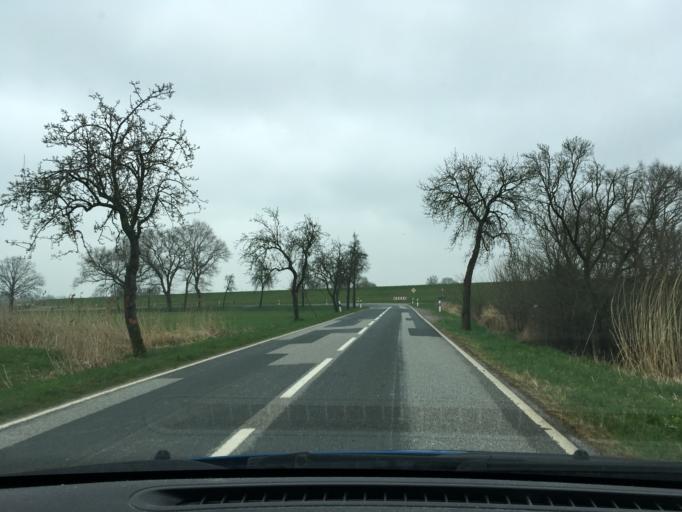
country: DE
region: Lower Saxony
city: Tosterglope
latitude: 53.2864
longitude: 10.8109
